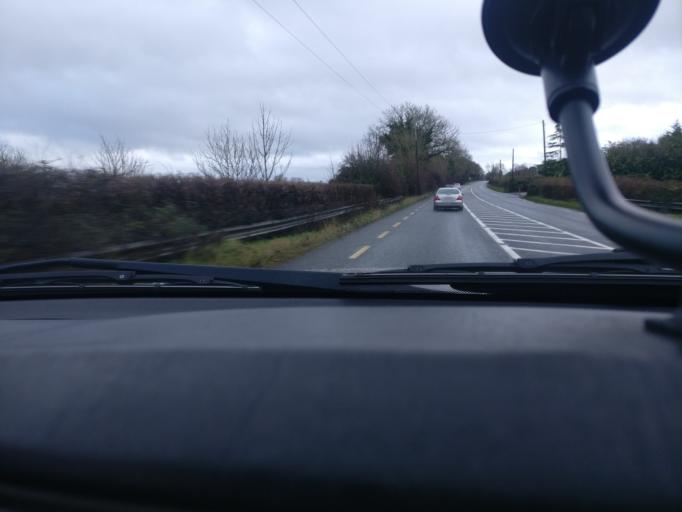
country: IE
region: Leinster
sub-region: Kildare
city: Kilcock
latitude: 53.4194
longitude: -6.7335
